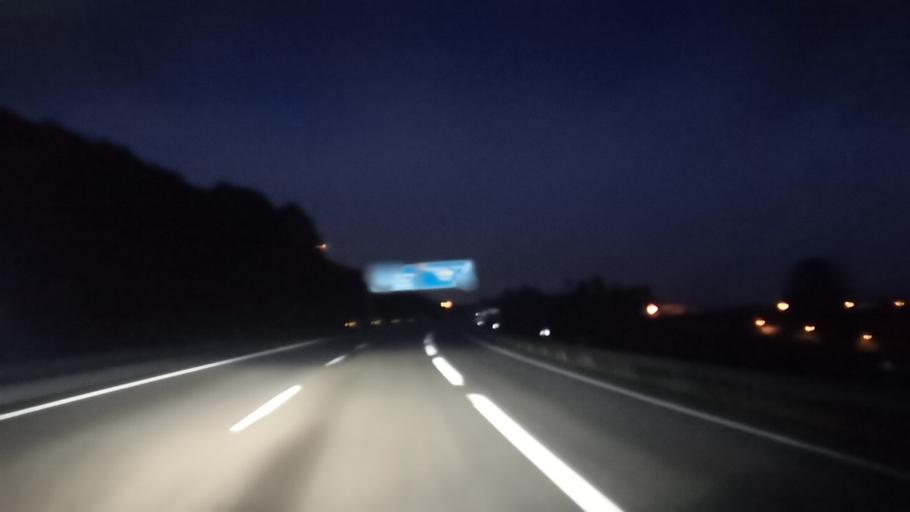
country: PT
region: Porto
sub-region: Felgueiras
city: Vizela
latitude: 41.3379
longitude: -8.2550
